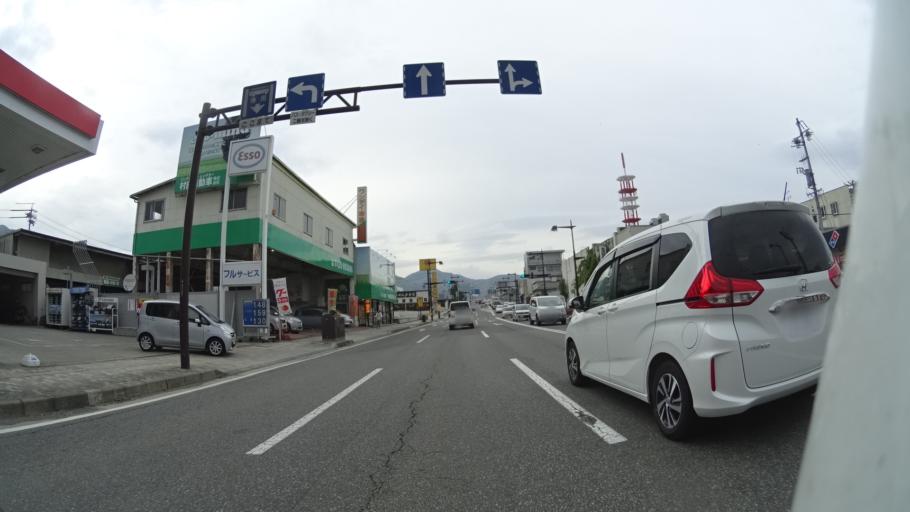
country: JP
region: Nagano
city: Nagano-shi
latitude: 36.6361
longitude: 138.1817
